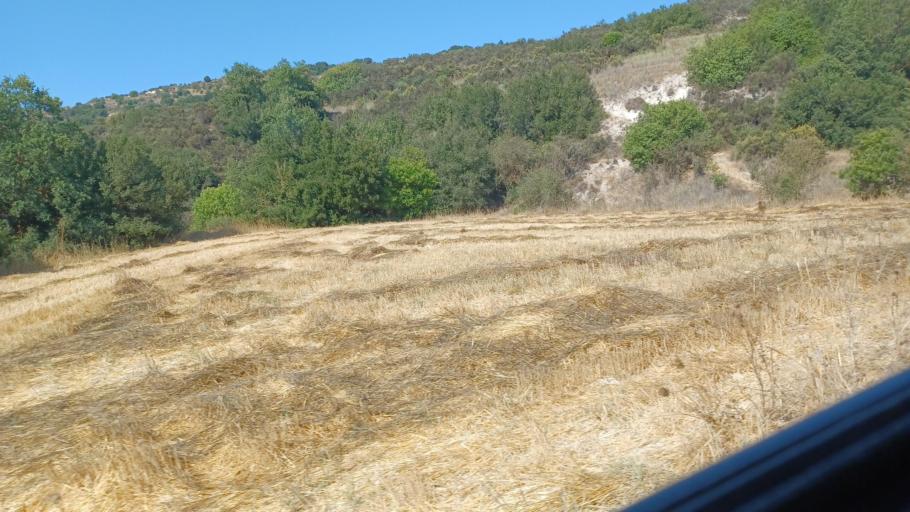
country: CY
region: Pafos
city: Mesogi
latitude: 34.8834
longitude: 32.5326
